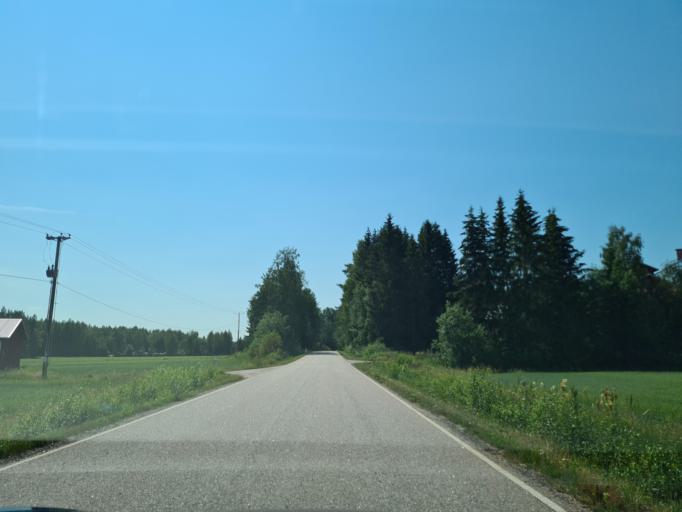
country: FI
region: Varsinais-Suomi
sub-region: Loimaa
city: Aura
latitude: 60.6045
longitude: 22.6070
